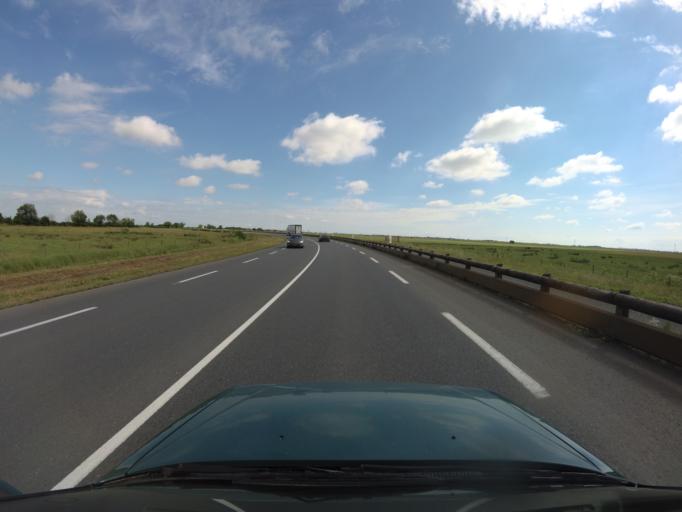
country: FR
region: Pays de la Loire
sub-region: Departement de la Vendee
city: Champagne-les-Marais
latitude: 46.4194
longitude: -1.1025
